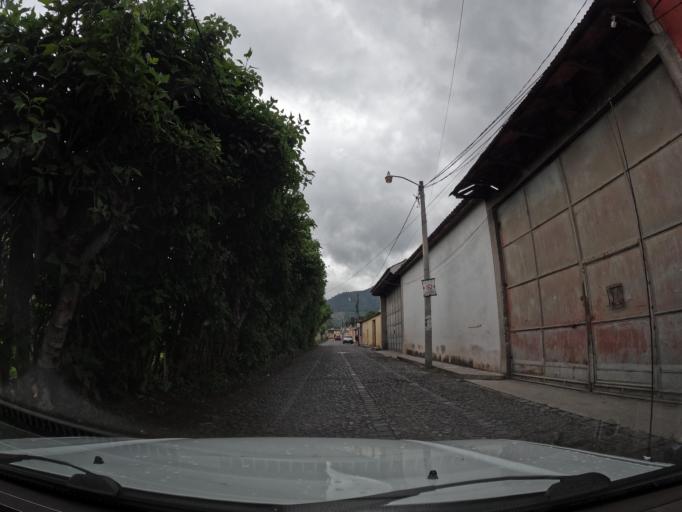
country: GT
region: Sacatepequez
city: Antigua Guatemala
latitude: 14.5651
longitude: -90.7405
